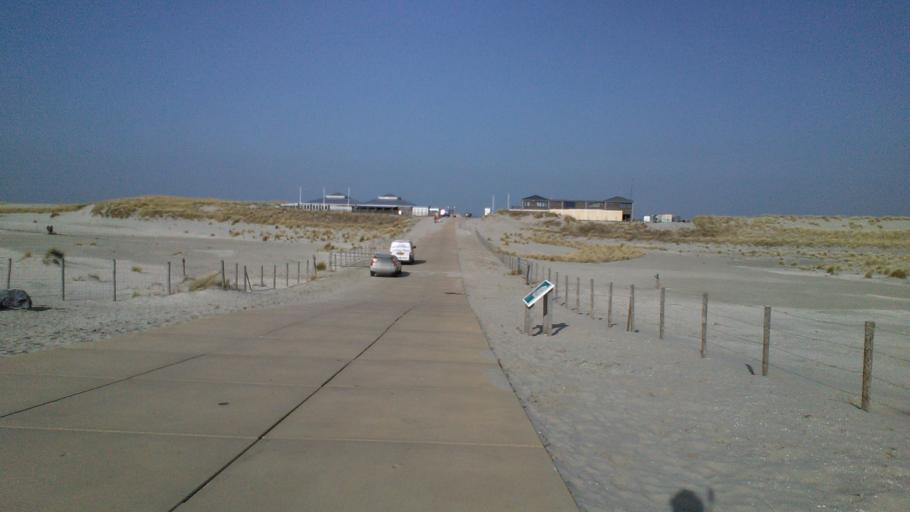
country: NL
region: South Holland
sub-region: Gemeente Rotterdam
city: Hoek van Holland
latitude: 52.0015
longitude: 4.1306
